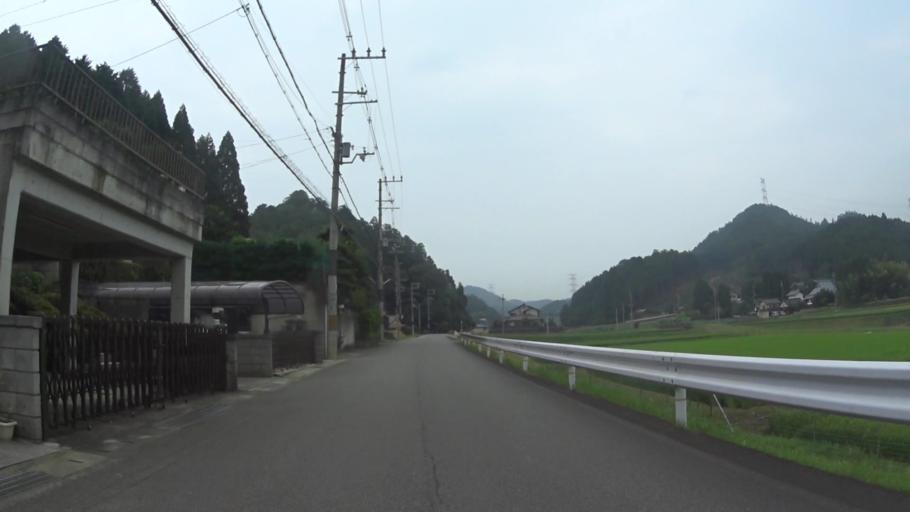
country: JP
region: Kyoto
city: Kameoka
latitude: 35.1661
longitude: 135.6071
